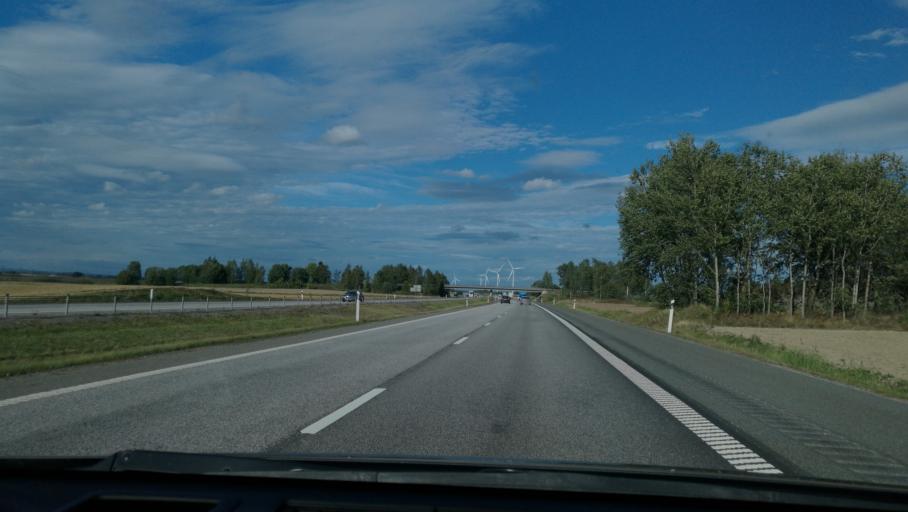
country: SE
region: OErebro
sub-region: Kumla Kommun
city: Kumla
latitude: 59.1490
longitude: 15.0960
